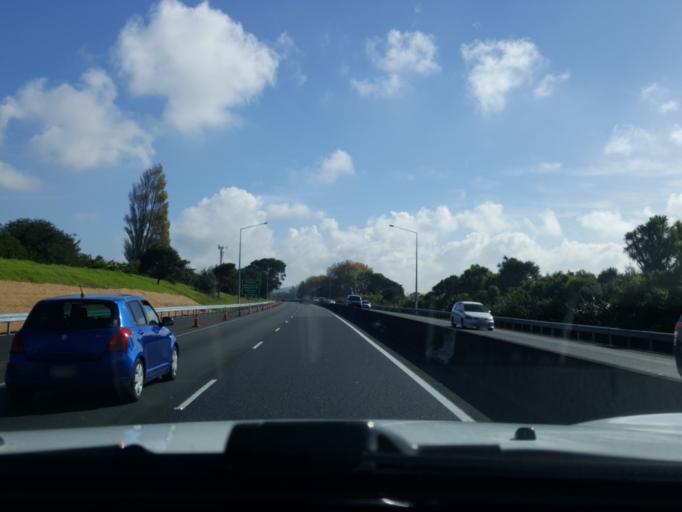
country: NZ
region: Auckland
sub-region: Auckland
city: Mangere
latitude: -36.9795
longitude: 174.8265
